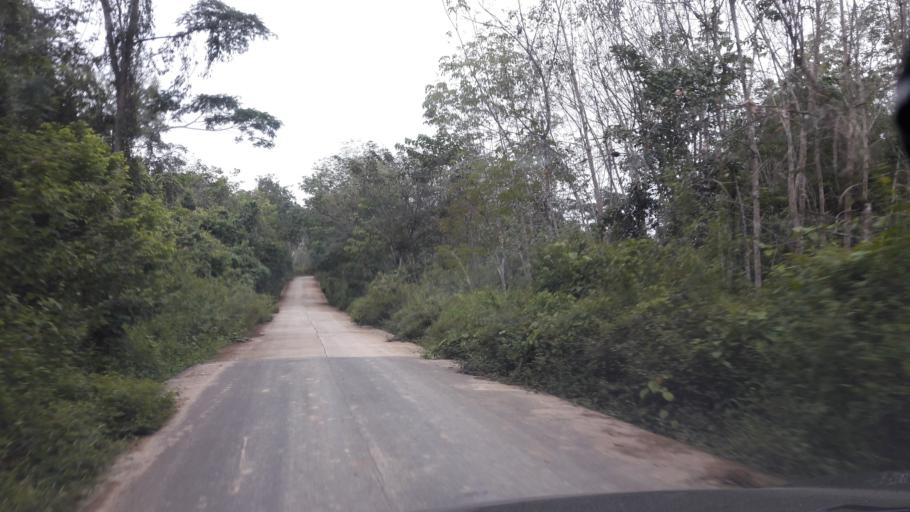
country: ID
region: South Sumatra
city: Gunungmenang
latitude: -3.1884
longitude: 103.8041
